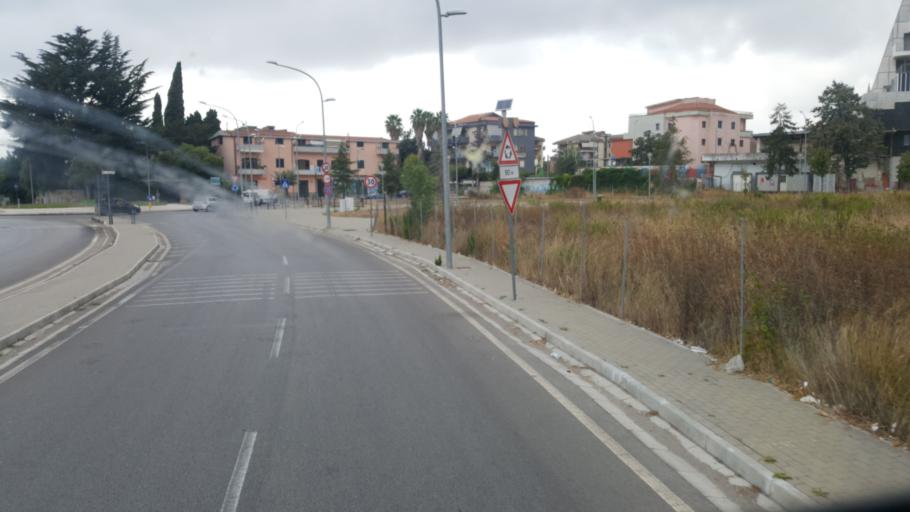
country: IT
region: Campania
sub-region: Provincia di Salerno
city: Battipaglia
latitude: 40.6029
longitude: 14.9830
